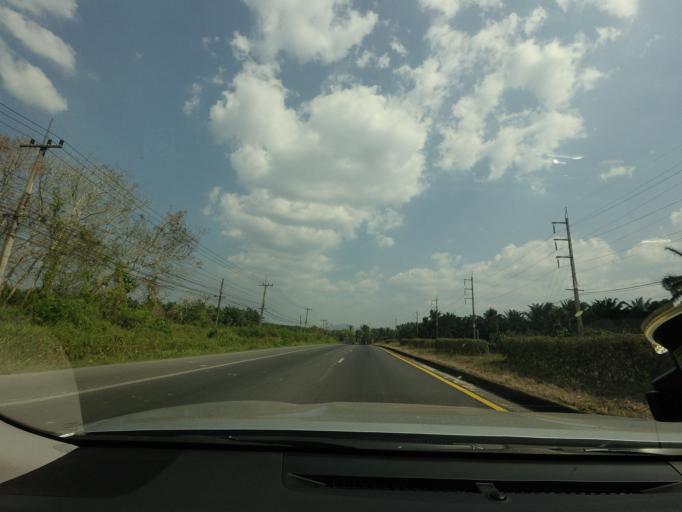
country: TH
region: Phangnga
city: Thap Put
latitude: 8.5103
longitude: 98.6466
